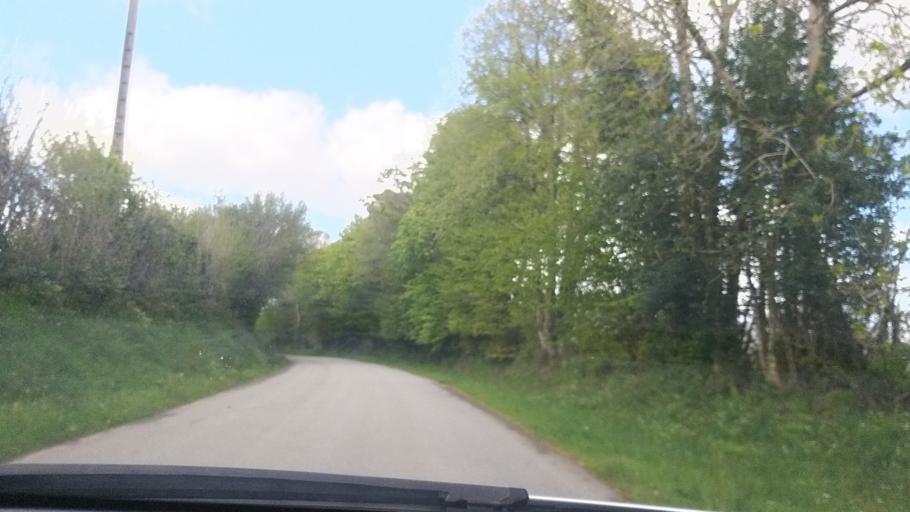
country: FR
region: Brittany
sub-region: Departement du Finistere
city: Huelgoat
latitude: 48.3476
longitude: -3.7293
